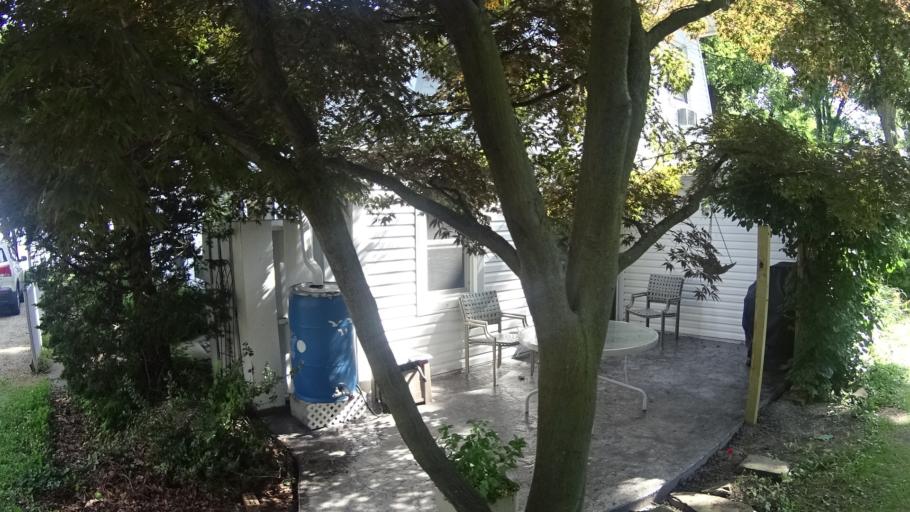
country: US
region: Ohio
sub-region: Erie County
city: Huron
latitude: 41.3833
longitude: -82.4701
